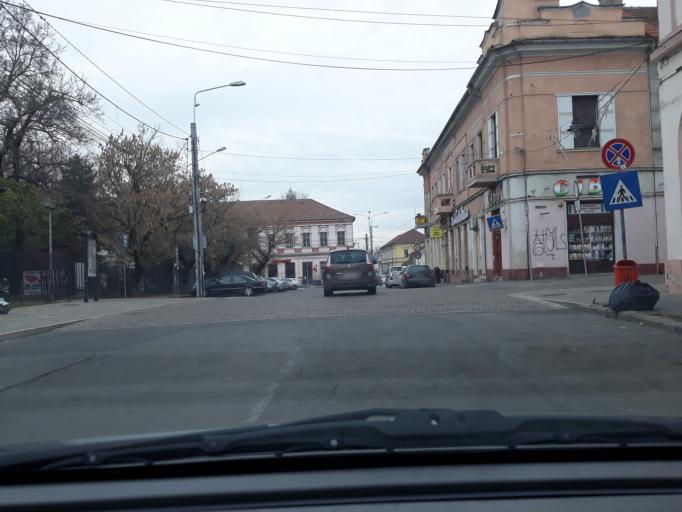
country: RO
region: Bihor
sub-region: Comuna Biharea
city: Oradea
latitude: 47.0537
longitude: 21.9329
